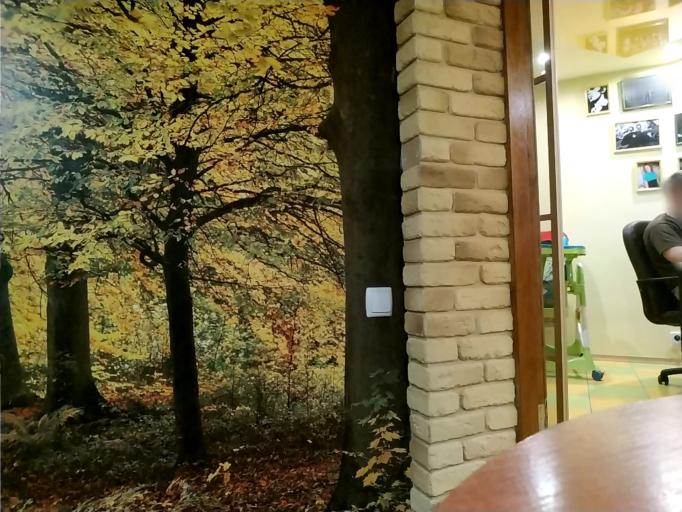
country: RU
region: Tverskaya
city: Zapadnaya Dvina
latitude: 56.3266
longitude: 31.9037
